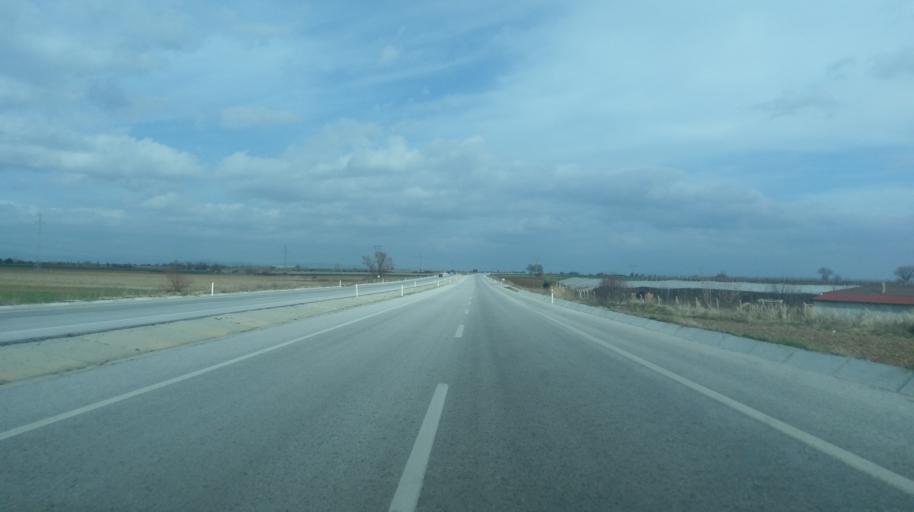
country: TR
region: Kirklareli
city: Inece
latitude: 41.6838
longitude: 27.1149
